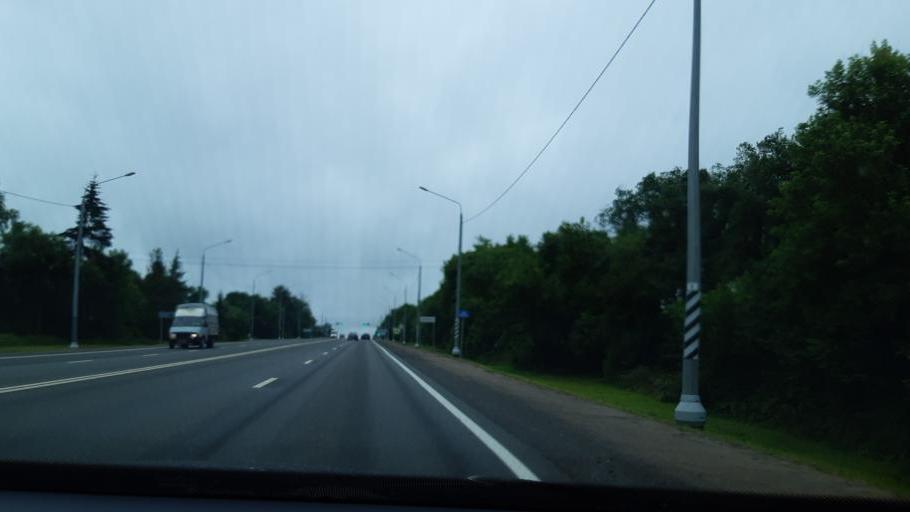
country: RU
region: Smolensk
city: Talashkino
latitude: 54.7141
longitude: 32.1100
